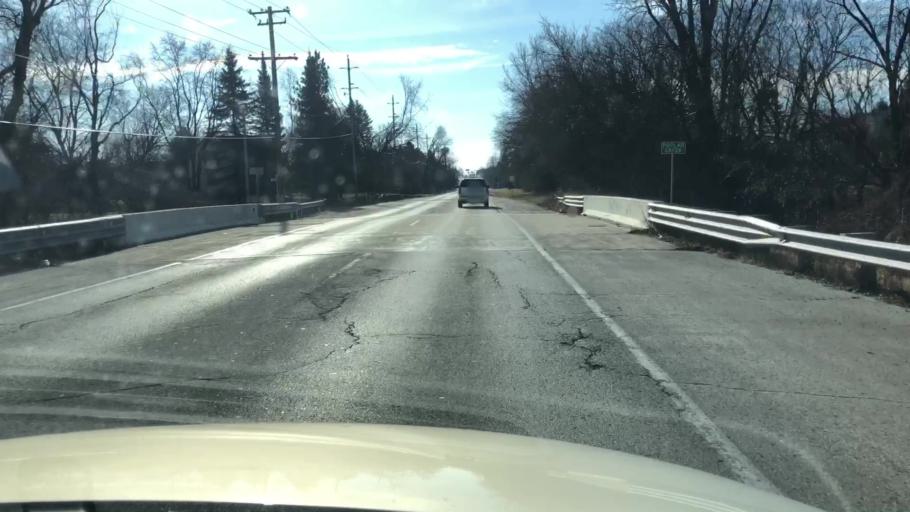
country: US
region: Wisconsin
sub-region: Waukesha County
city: Brookfield
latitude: 43.0446
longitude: -88.1666
